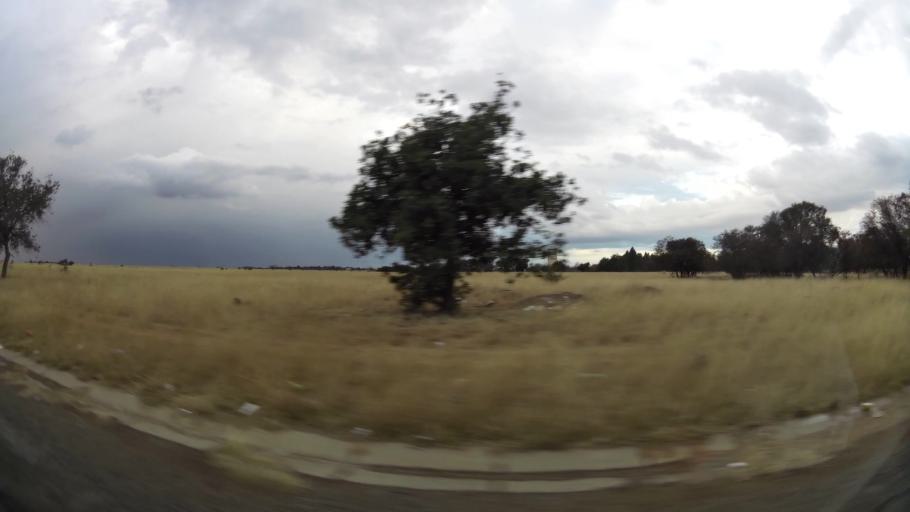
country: ZA
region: Orange Free State
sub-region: Lejweleputswa District Municipality
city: Welkom
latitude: -27.9488
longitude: 26.7349
